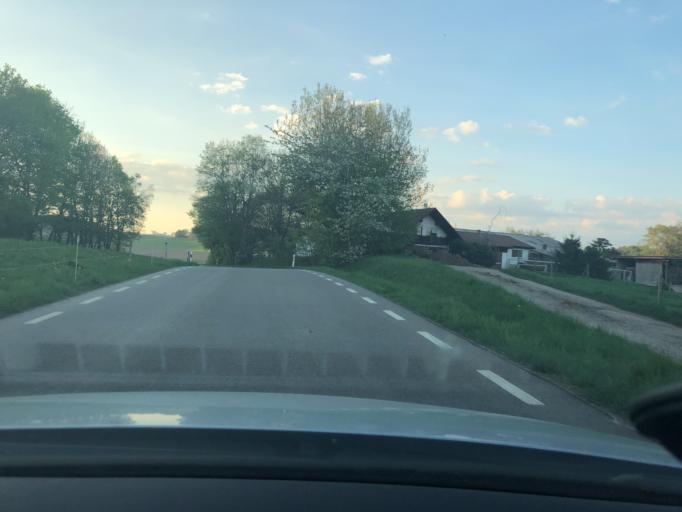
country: DE
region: Baden-Wuerttemberg
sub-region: Freiburg Region
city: Dogern
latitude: 47.6542
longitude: 8.1782
